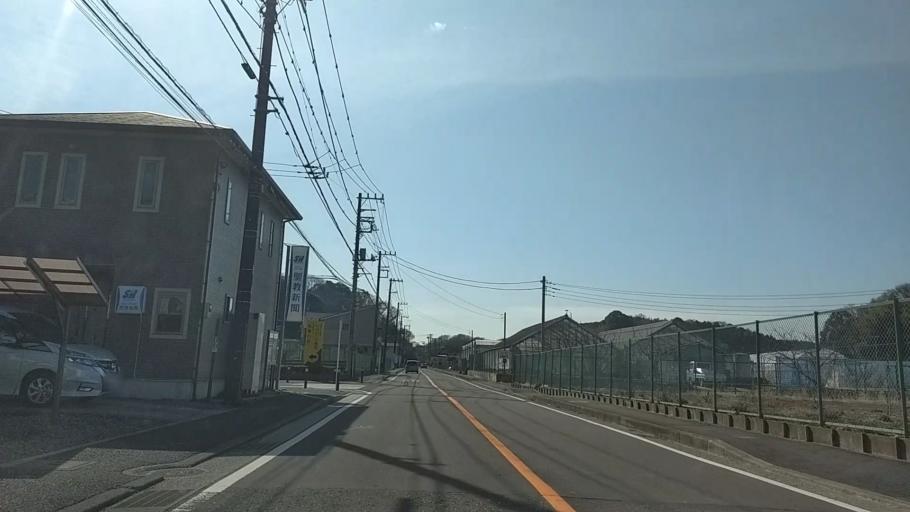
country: JP
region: Kanagawa
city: Kamakura
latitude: 35.4065
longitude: 139.5527
